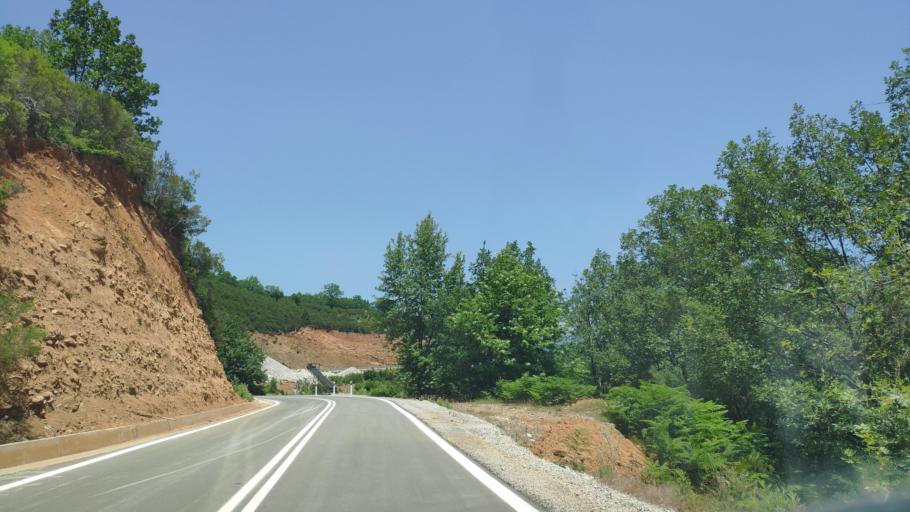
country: GR
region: Epirus
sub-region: Nomos Artas
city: Ano Kalentini
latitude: 39.1889
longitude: 21.3496
